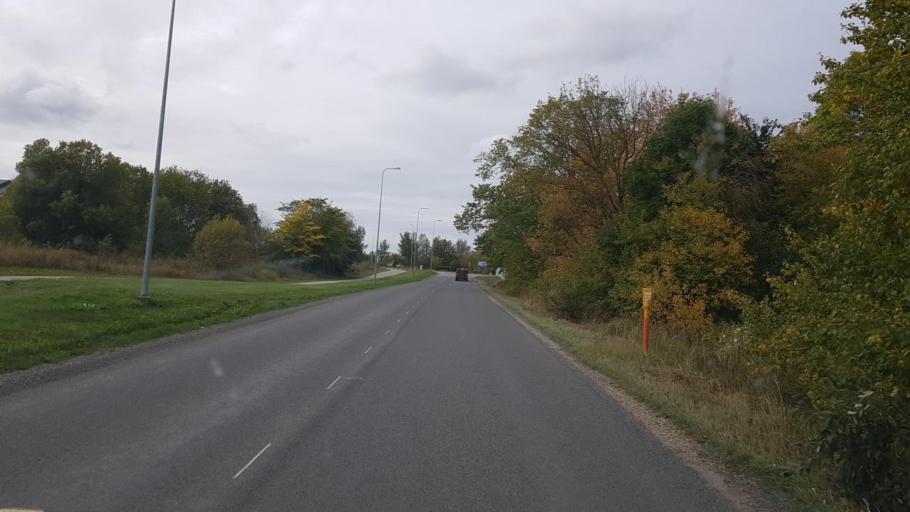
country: EE
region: Laeaene-Virumaa
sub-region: Rakvere linn
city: Rakvere
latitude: 59.3636
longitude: 26.3450
